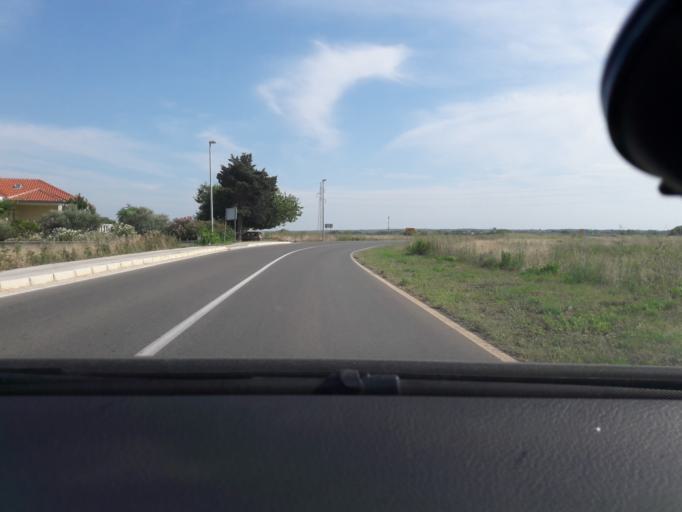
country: HR
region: Zadarska
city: Nin
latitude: 44.2348
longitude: 15.1820
